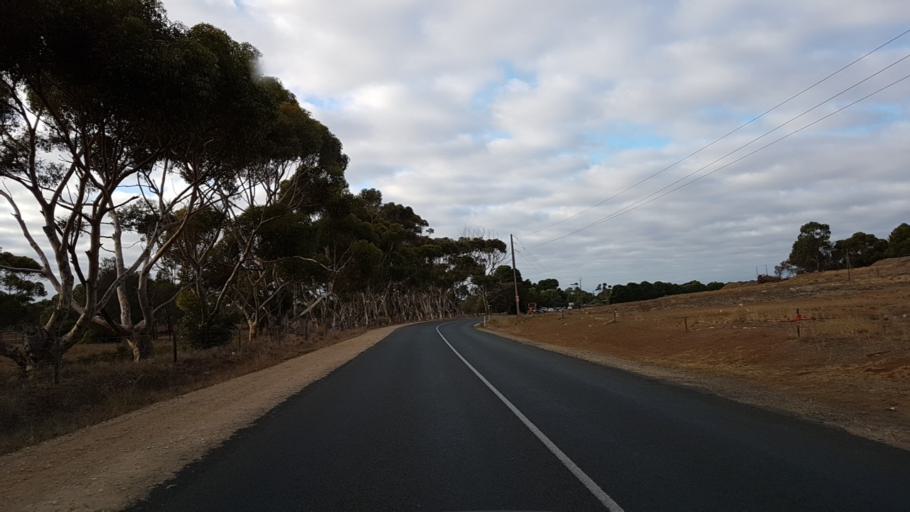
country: AU
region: South Australia
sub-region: Alexandrina
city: Strathalbyn
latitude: -35.2676
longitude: 138.9081
